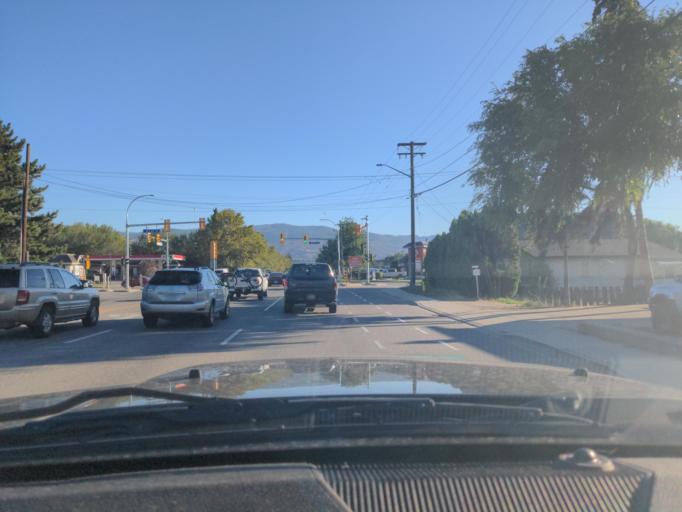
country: CA
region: British Columbia
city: Kelowna
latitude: 49.8616
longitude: -119.4744
